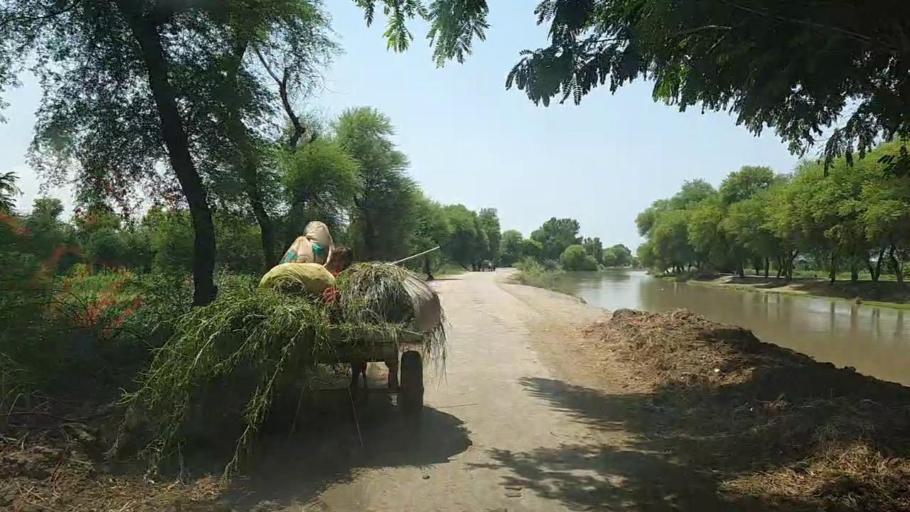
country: PK
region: Sindh
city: Ubauro
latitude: 28.1448
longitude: 69.7760
